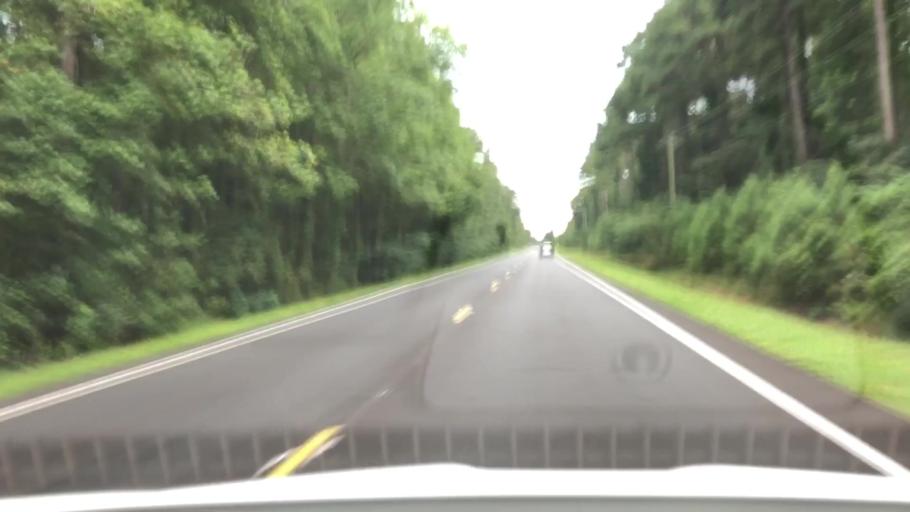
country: US
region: North Carolina
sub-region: Jones County
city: Maysville
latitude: 34.8744
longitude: -77.1994
